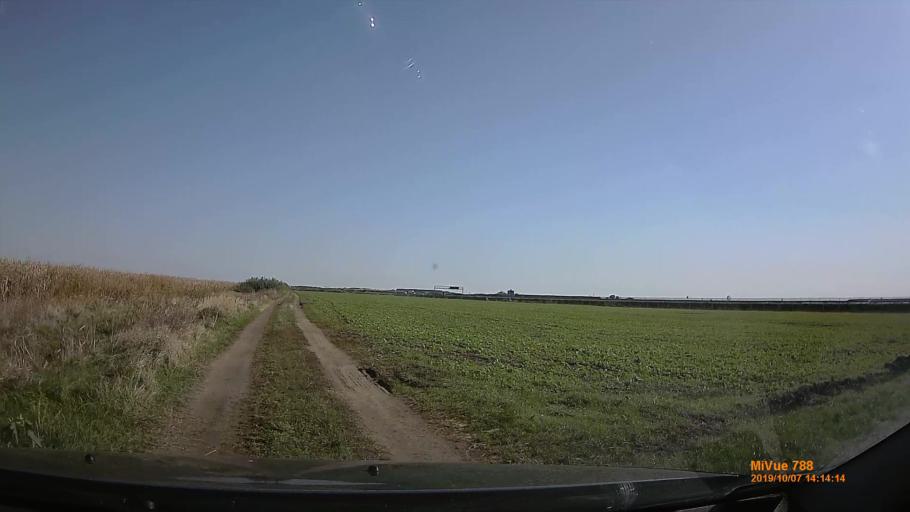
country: HU
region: Jasz-Nagykun-Szolnok
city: Kunszentmarton
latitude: 46.8809
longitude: 20.2475
